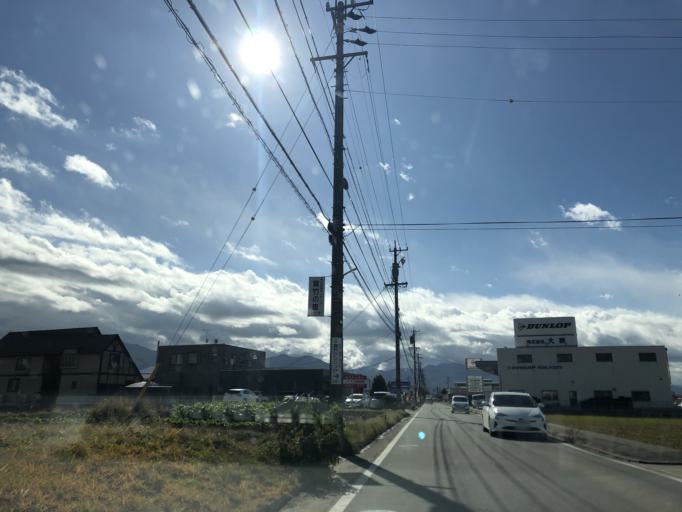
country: JP
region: Nagano
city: Suzaka
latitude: 36.6735
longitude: 138.2582
